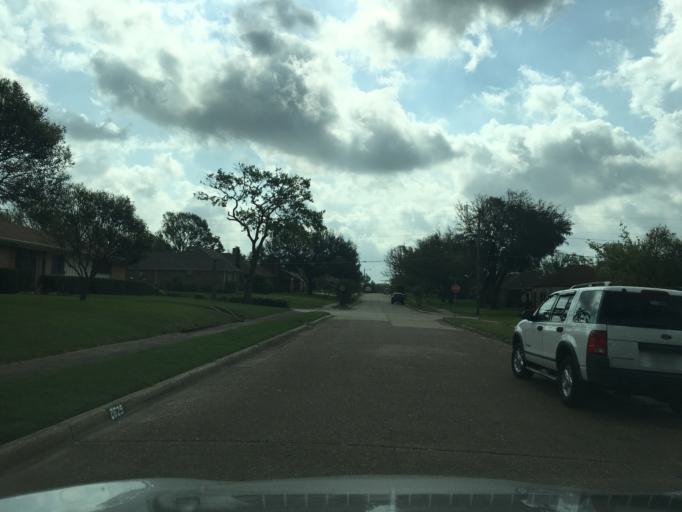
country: US
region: Texas
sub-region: Dallas County
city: Richardson
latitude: 32.9030
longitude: -96.7550
